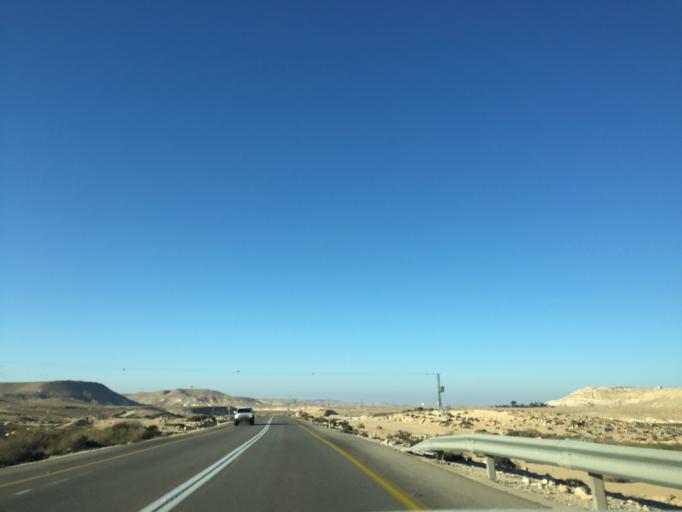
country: IL
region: Southern District
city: Midreshet Ben-Gurion
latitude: 30.7737
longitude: 34.7714
